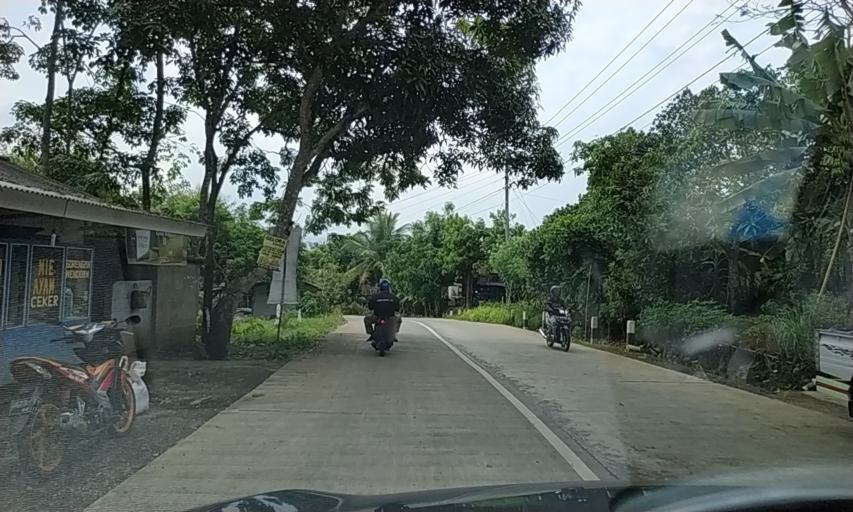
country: ID
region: Central Java
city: Winangun
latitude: -7.3641
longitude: 108.7014
